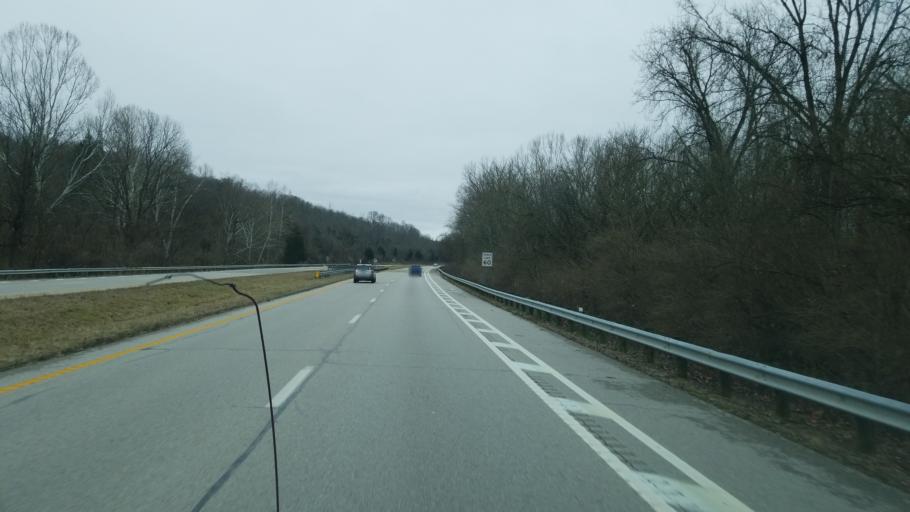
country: US
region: Ohio
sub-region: Clermont County
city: Withamsville
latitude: 39.0086
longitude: -84.3025
